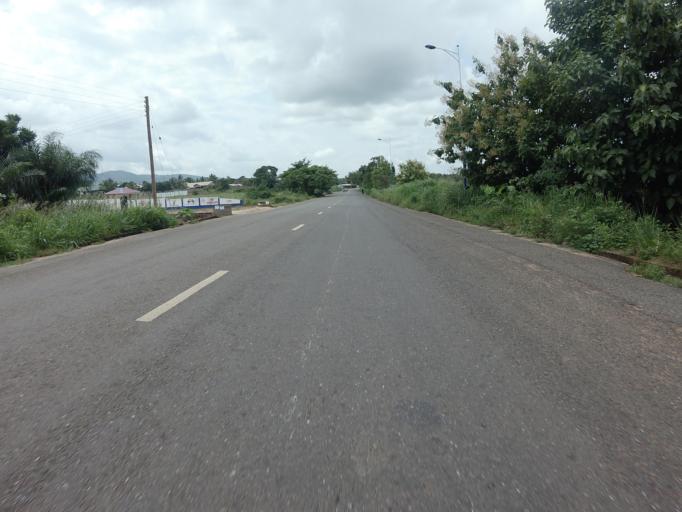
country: GH
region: Volta
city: Ho
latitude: 6.6188
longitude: 0.4944
